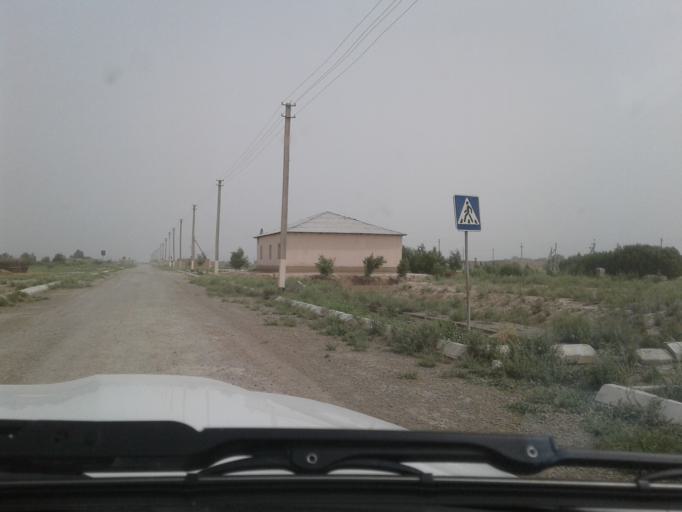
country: TM
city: Akdepe
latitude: 41.5977
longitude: 58.6067
